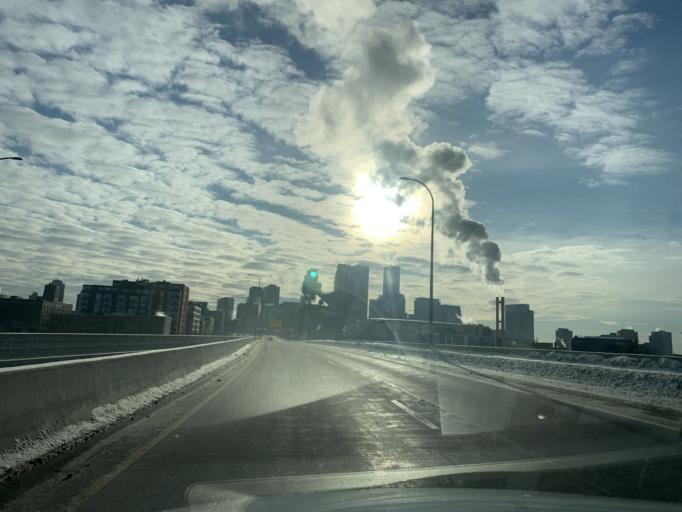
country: US
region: Minnesota
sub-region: Hennepin County
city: Minneapolis
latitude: 44.9884
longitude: -93.2831
